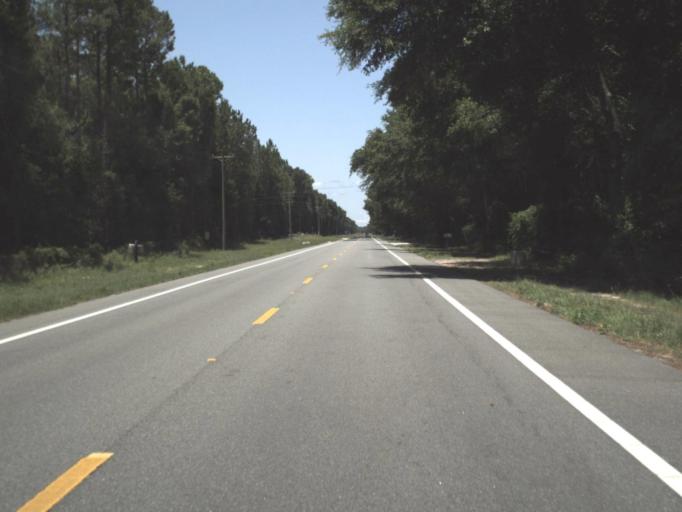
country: US
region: Florida
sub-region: Dixie County
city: Cross City
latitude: 29.7221
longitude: -82.9845
